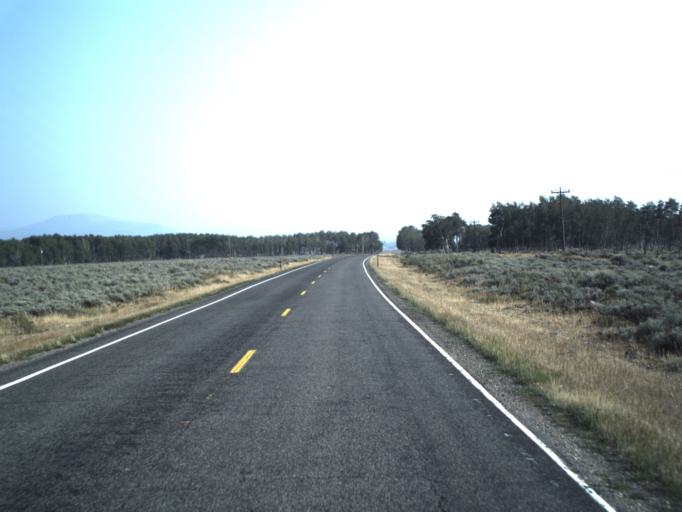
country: US
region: Wyoming
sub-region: Uinta County
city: Evanston
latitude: 40.9680
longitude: -110.8479
